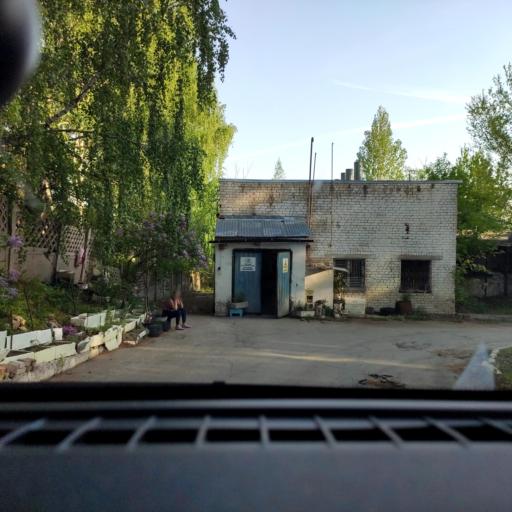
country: RU
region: Samara
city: Tol'yatti
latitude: 53.4755
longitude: 49.3570
